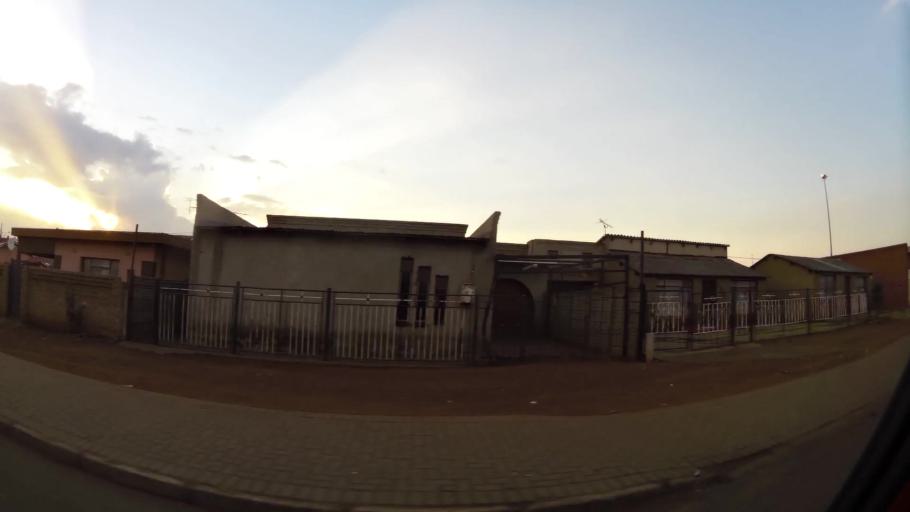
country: ZA
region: Gauteng
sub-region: City of Johannesburg Metropolitan Municipality
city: Orange Farm
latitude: -26.5720
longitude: 27.8397
